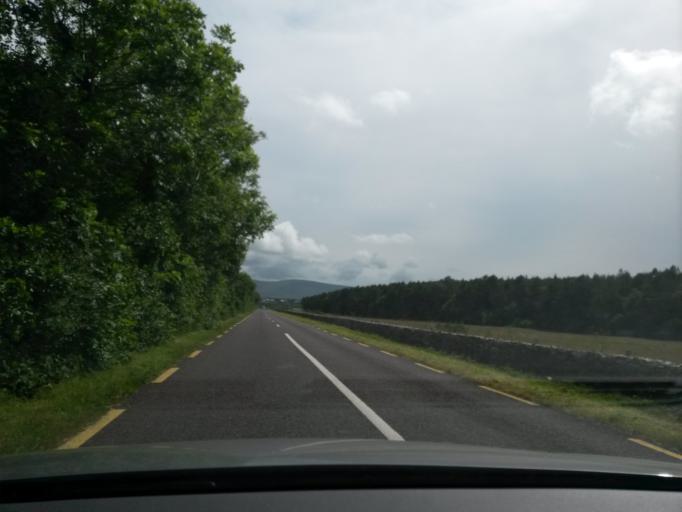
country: IE
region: Connaught
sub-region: County Leitrim
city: Kinlough
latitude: 54.4484
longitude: -8.4543
